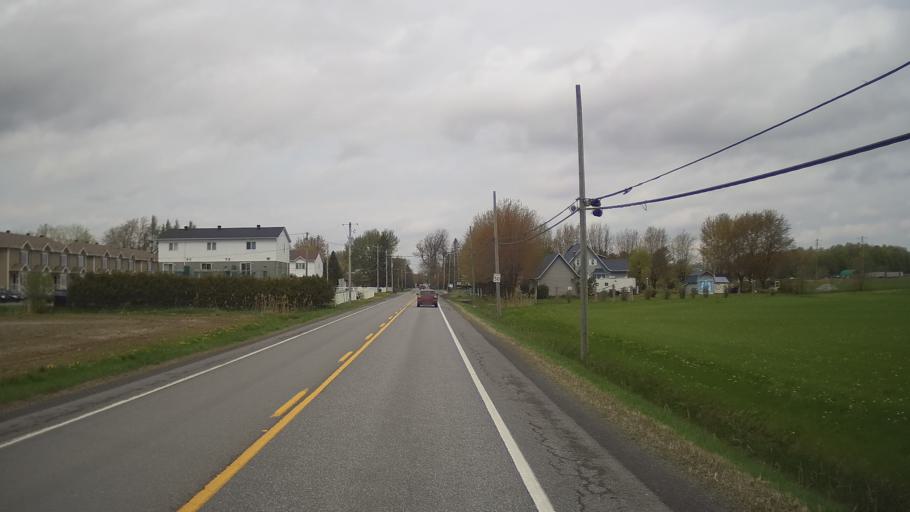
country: CA
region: Quebec
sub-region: Monteregie
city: Marieville
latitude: 45.3323
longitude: -73.1538
